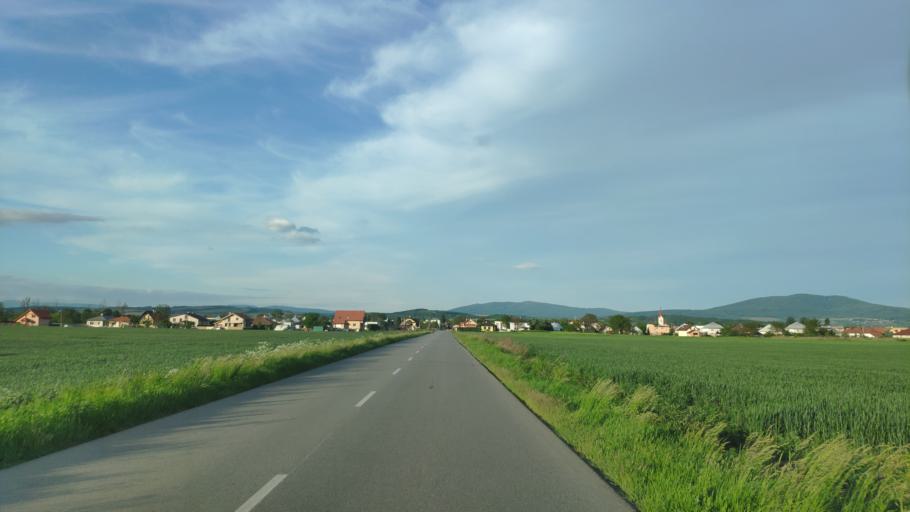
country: SK
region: Kosicky
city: Kosice
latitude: 48.6461
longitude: 21.3148
